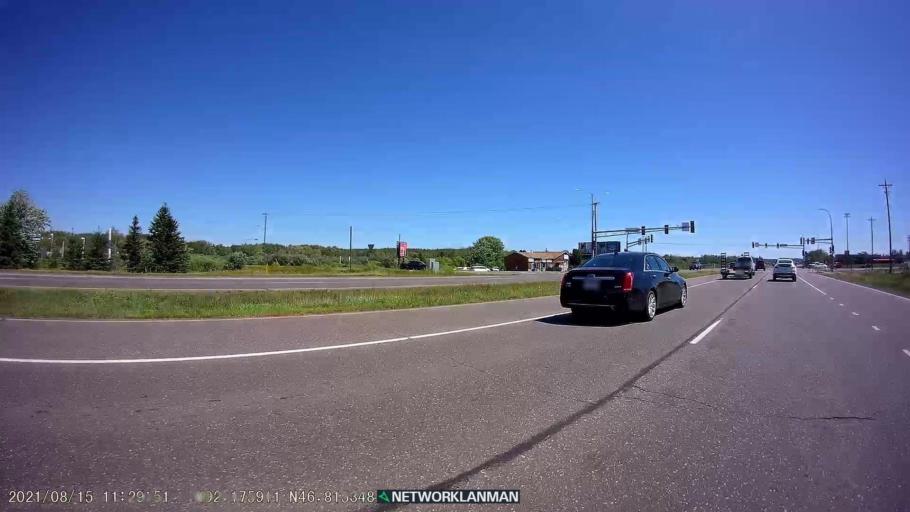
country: US
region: Minnesota
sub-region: Saint Louis County
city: Hermantown
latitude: 46.8151
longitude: -92.1760
